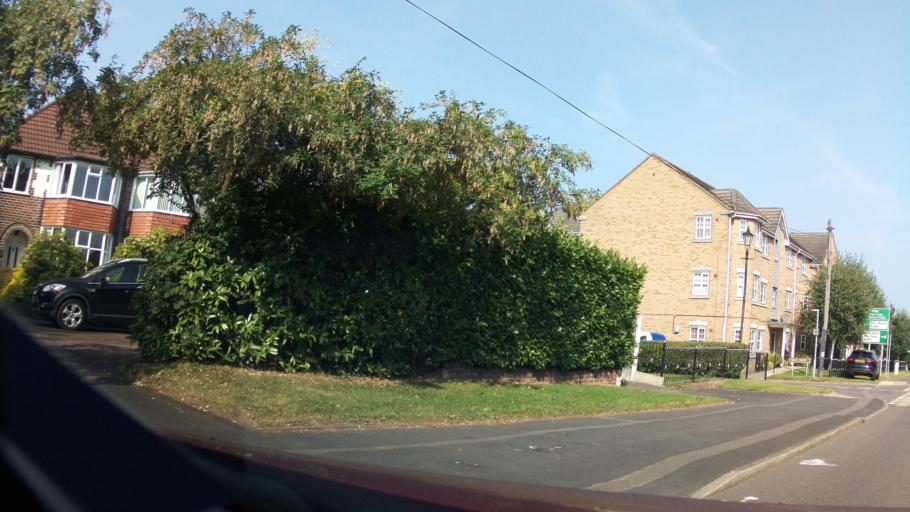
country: GB
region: England
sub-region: Walsall
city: Streetly
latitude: 52.5824
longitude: -1.8862
